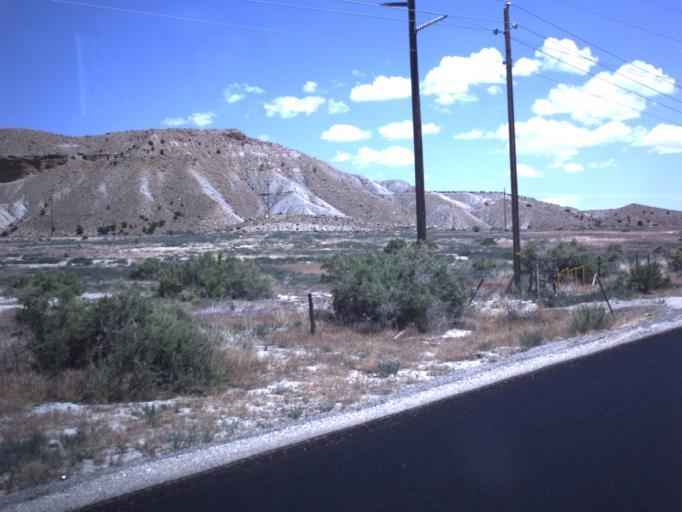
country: US
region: Utah
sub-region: Emery County
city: Orangeville
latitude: 39.2571
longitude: -111.1017
